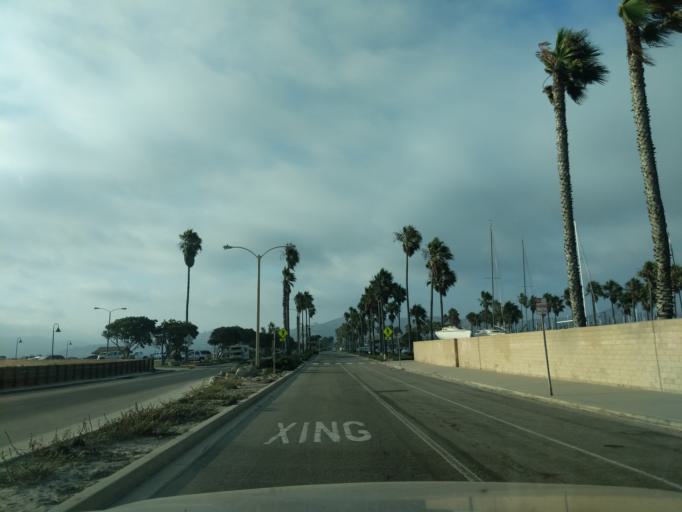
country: US
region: California
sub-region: Ventura County
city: Ventura
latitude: 34.2449
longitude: -119.2663
